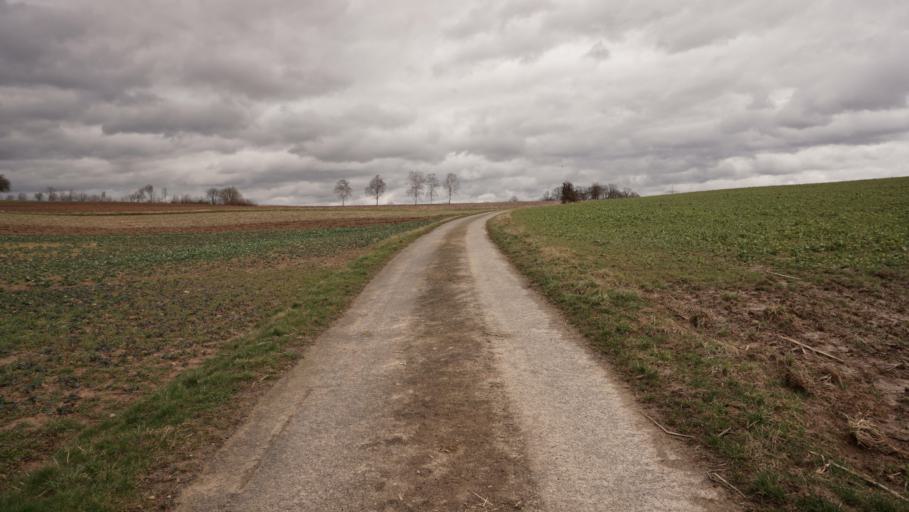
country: DE
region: Baden-Wuerttemberg
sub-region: Karlsruhe Region
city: Mosbach
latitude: 49.3613
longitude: 9.2028
